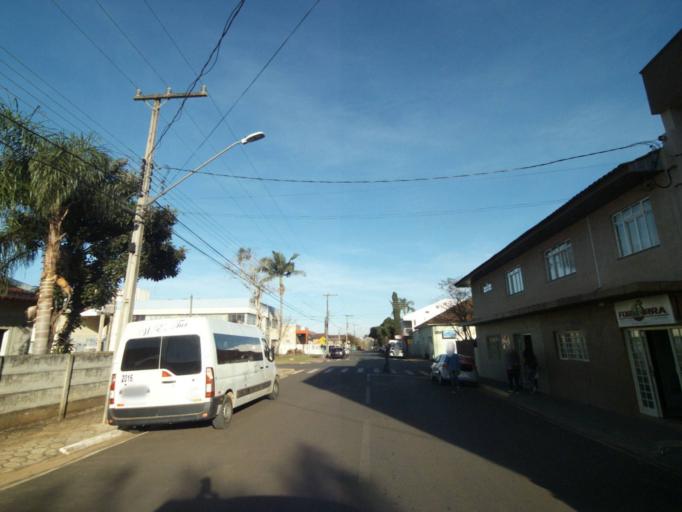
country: BR
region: Parana
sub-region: Tibagi
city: Tibagi
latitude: -24.5165
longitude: -50.4086
